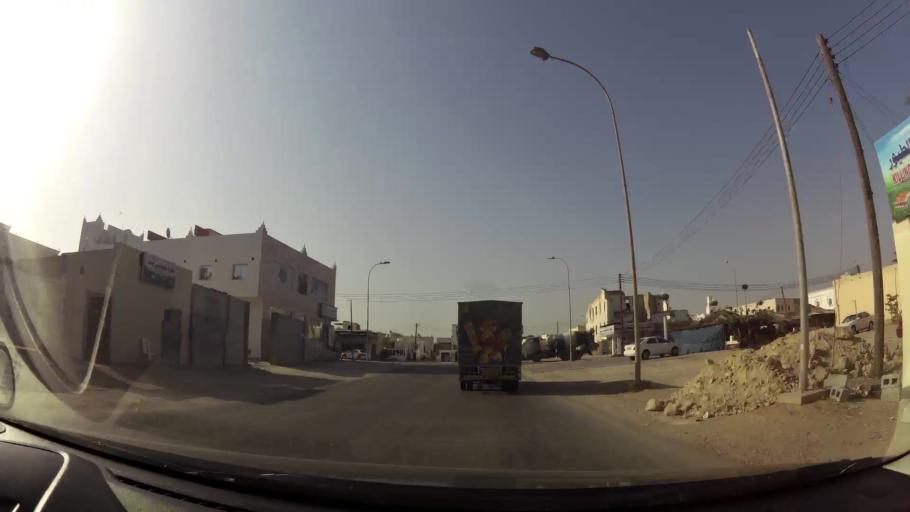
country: OM
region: Zufar
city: Salalah
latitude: 17.0089
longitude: 54.0980
